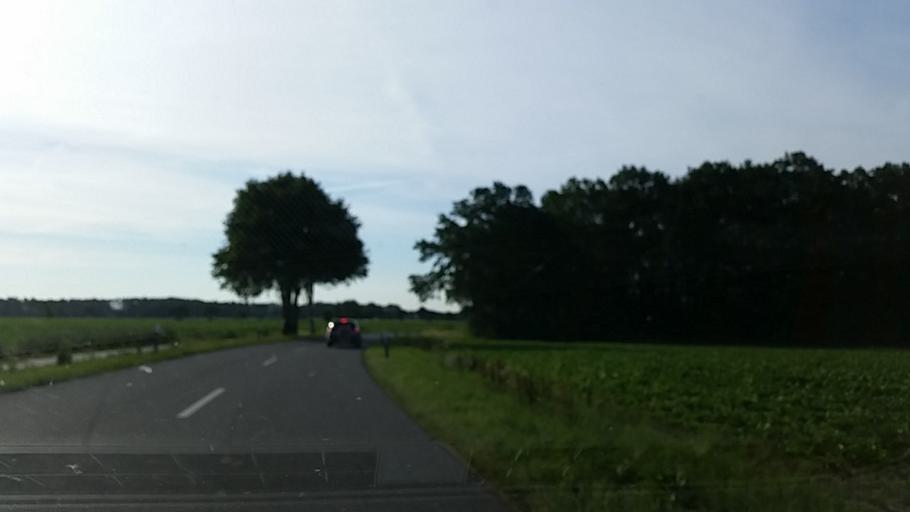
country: DE
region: Lower Saxony
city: Ratzlingen
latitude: 52.9372
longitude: 10.6379
